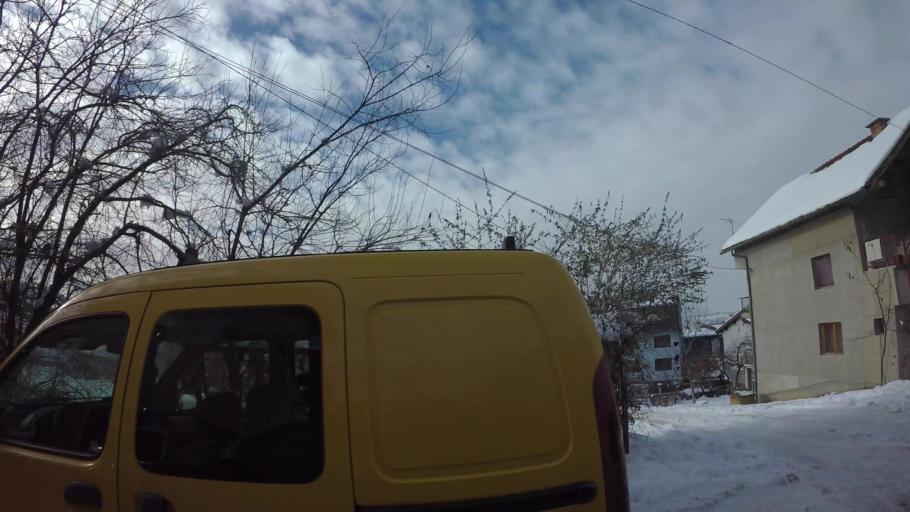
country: BA
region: Federation of Bosnia and Herzegovina
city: Kobilja Glava
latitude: 43.8777
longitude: 18.4175
